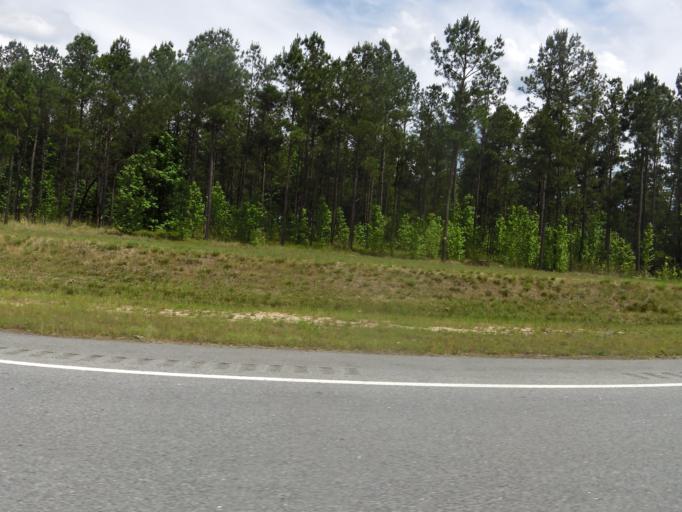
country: US
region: Georgia
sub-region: Jefferson County
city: Wadley
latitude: 32.7530
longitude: -82.3895
